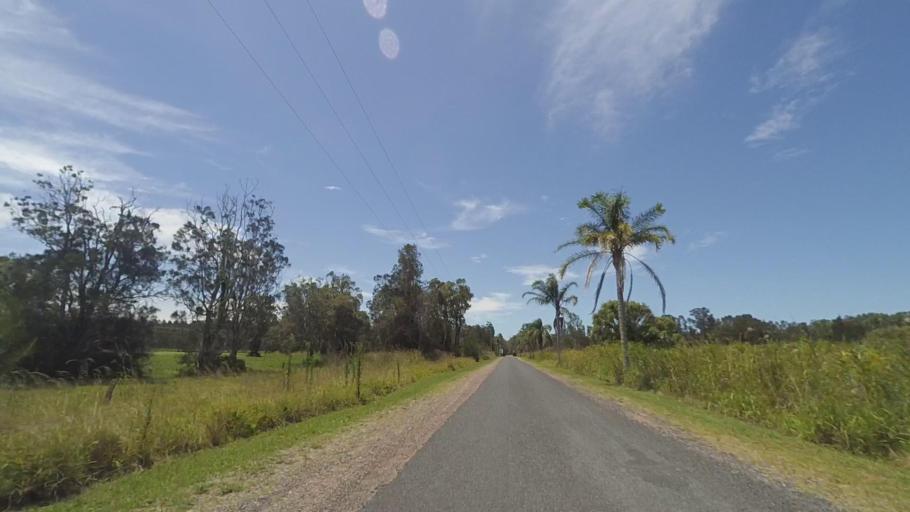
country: AU
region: New South Wales
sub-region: Port Stephens Shire
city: Anna Bay
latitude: -32.7697
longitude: 152.0022
